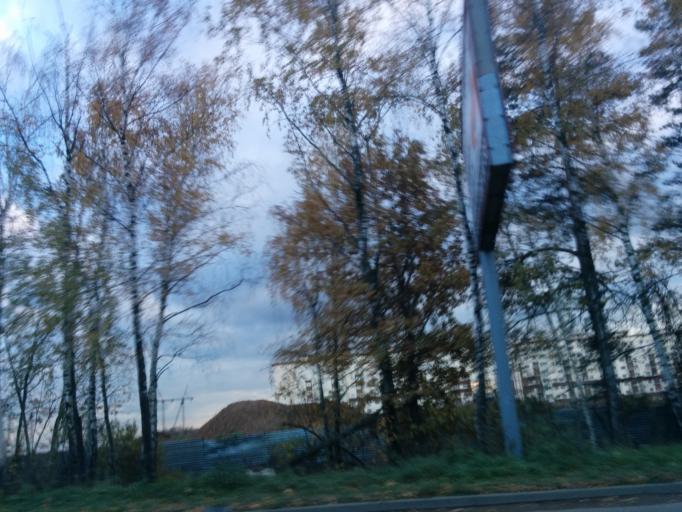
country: RU
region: Moscow
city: Zagor'ye
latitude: 55.5376
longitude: 37.6380
